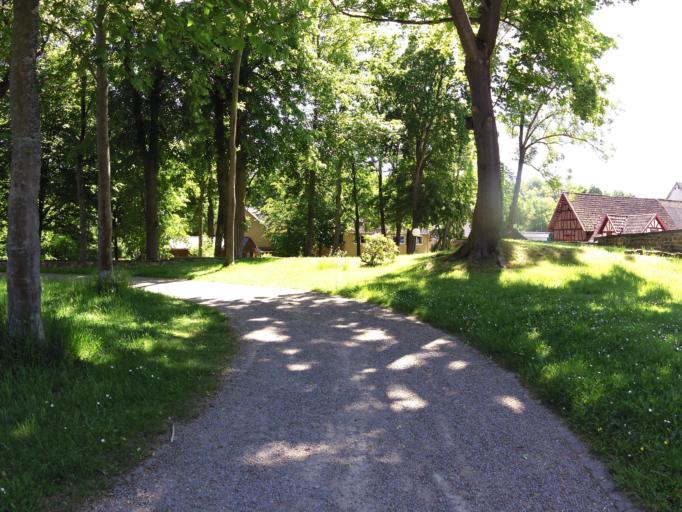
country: DE
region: Hesse
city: Philippsthal
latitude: 50.8403
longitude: 10.0034
